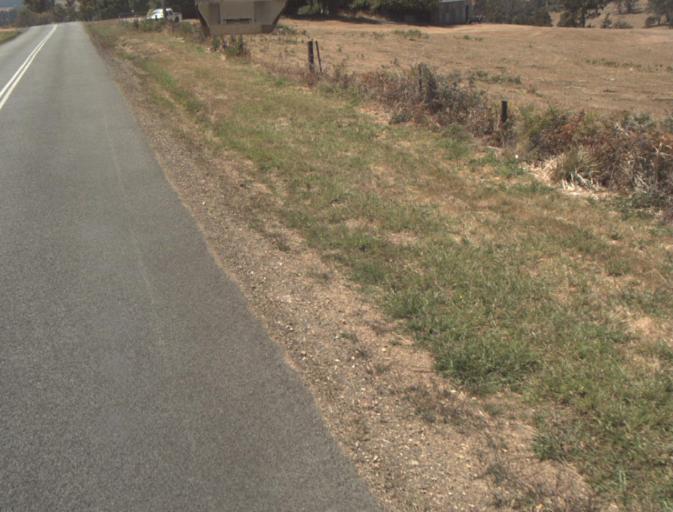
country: AU
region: Tasmania
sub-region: Launceston
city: Mayfield
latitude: -41.2736
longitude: 147.1272
